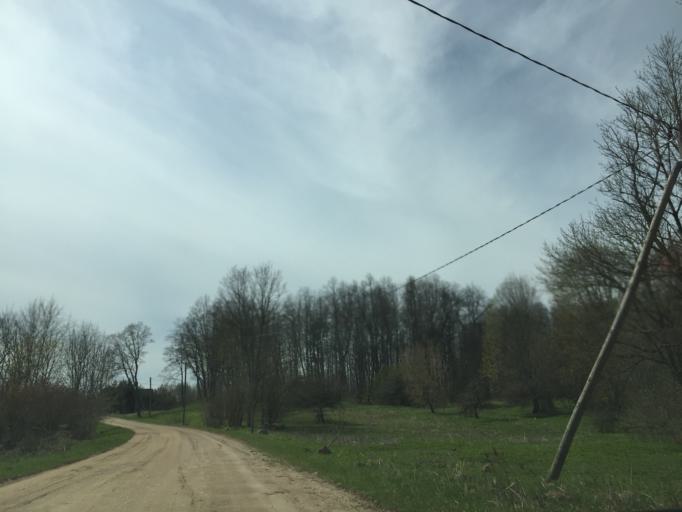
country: LV
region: Ludzas Rajons
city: Ludza
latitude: 56.5246
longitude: 27.5478
